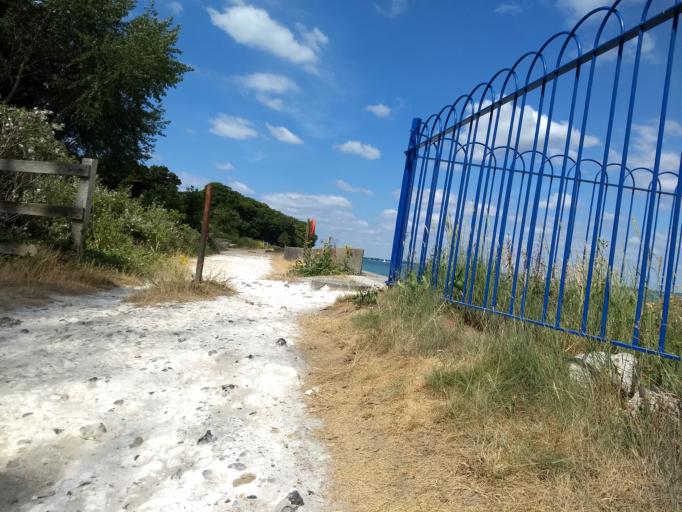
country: GB
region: England
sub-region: Isle of Wight
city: Yarmouth
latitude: 50.7061
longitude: -1.5104
